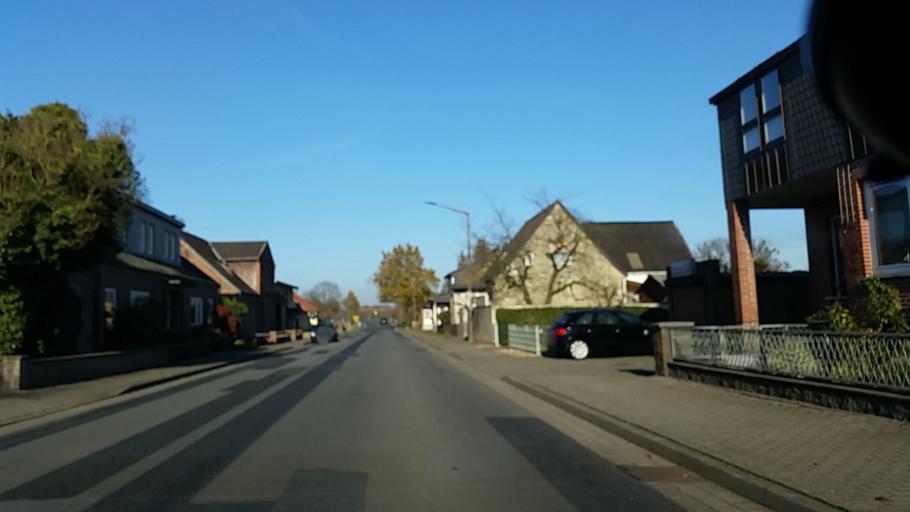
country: DE
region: Saxony-Anhalt
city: Jubar
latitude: 52.6501
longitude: 10.8617
